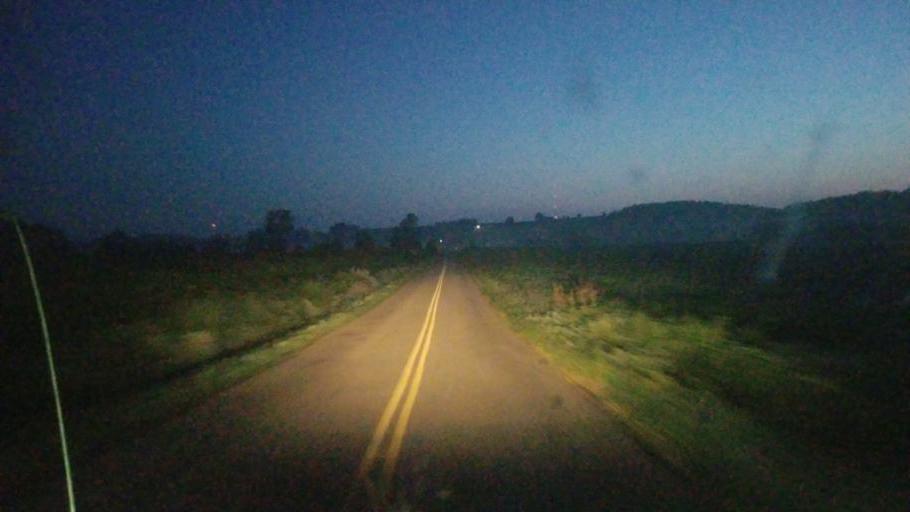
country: US
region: Ohio
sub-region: Perry County
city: Thornport
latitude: 39.9122
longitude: -82.3375
